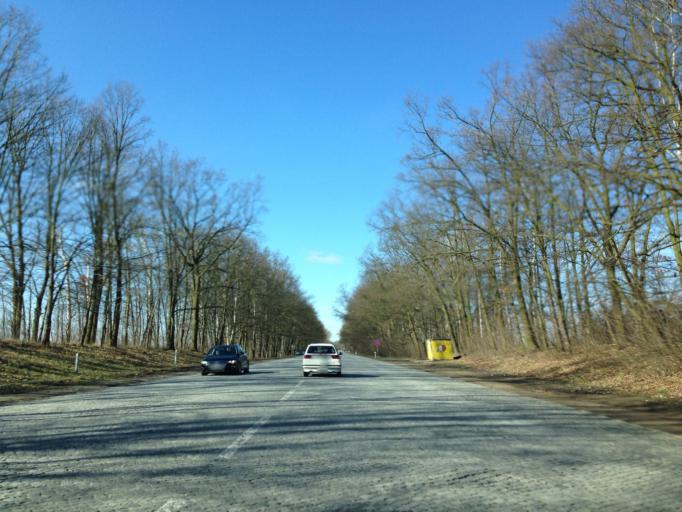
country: PL
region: Pomeranian Voivodeship
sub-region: Powiat tczewski
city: Tczew
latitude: 54.0494
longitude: 18.7876
